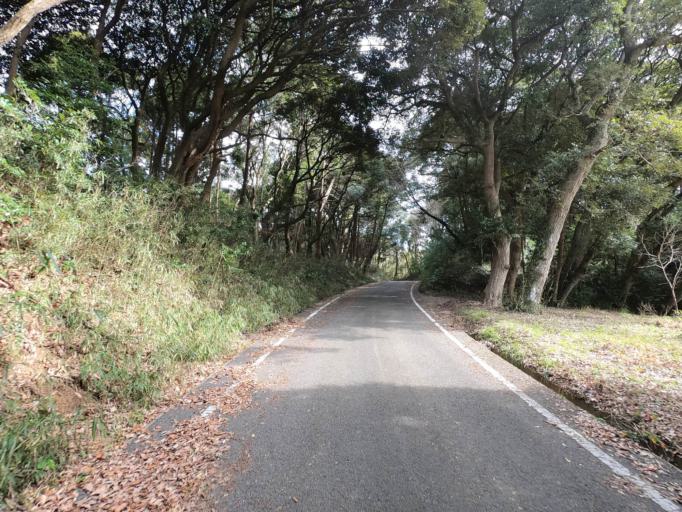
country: JP
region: Ibaraki
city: Inashiki
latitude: 36.0584
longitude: 140.4428
